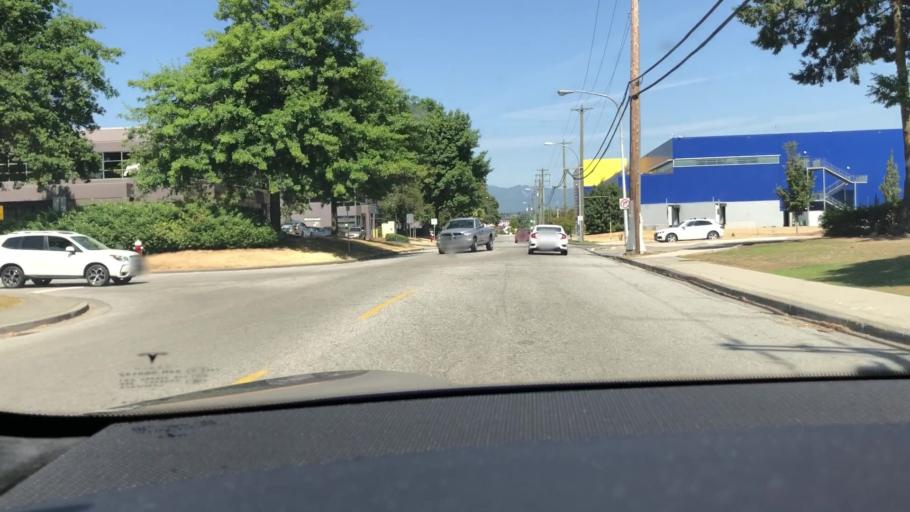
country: CA
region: British Columbia
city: Richmond
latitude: 49.1872
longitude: -123.0803
